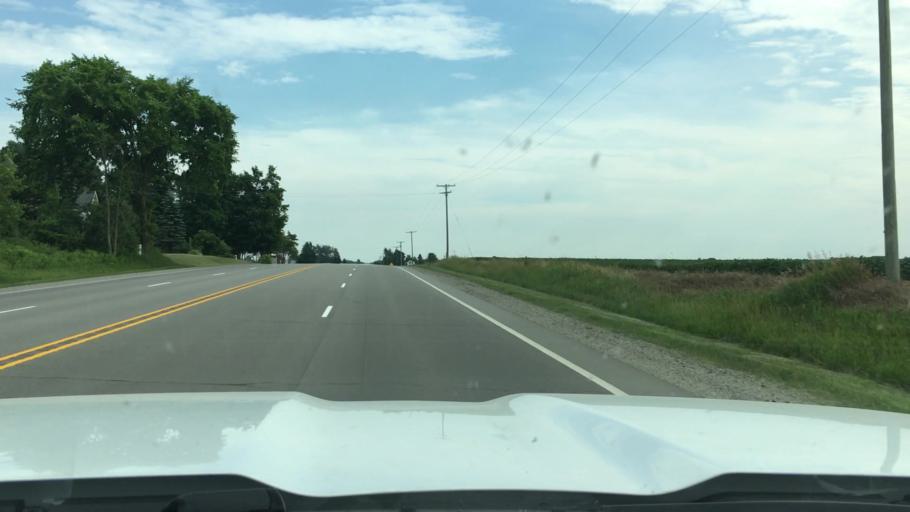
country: US
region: Michigan
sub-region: Sanilac County
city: Marlette
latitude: 43.3816
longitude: -83.0860
